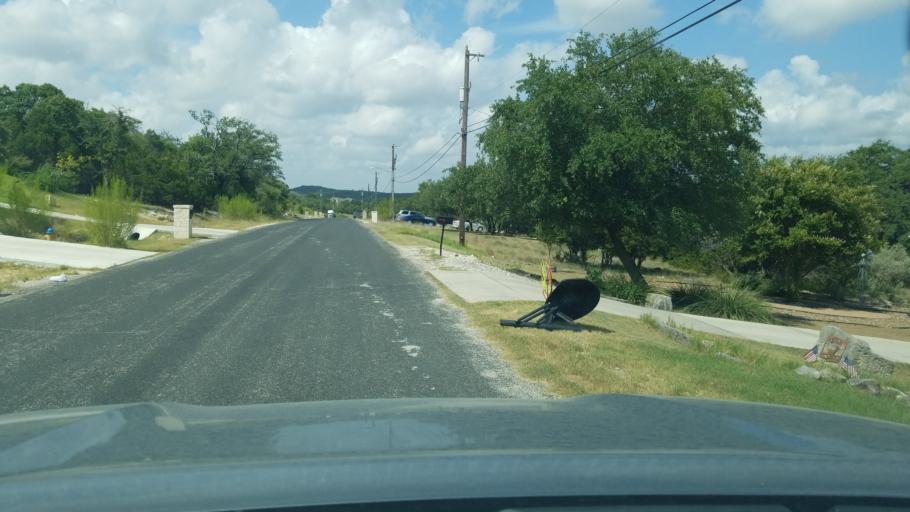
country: US
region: Texas
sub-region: Bexar County
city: Timberwood Park
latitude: 29.6817
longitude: -98.5168
